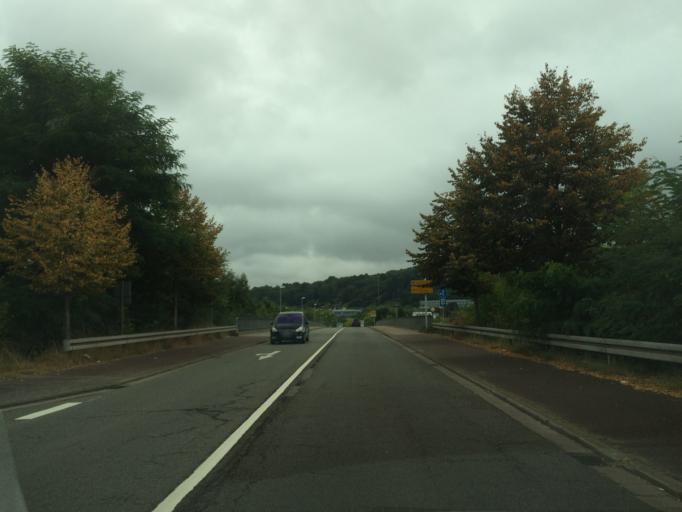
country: DE
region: Saarland
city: Merzig
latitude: 49.4417
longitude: 6.6279
